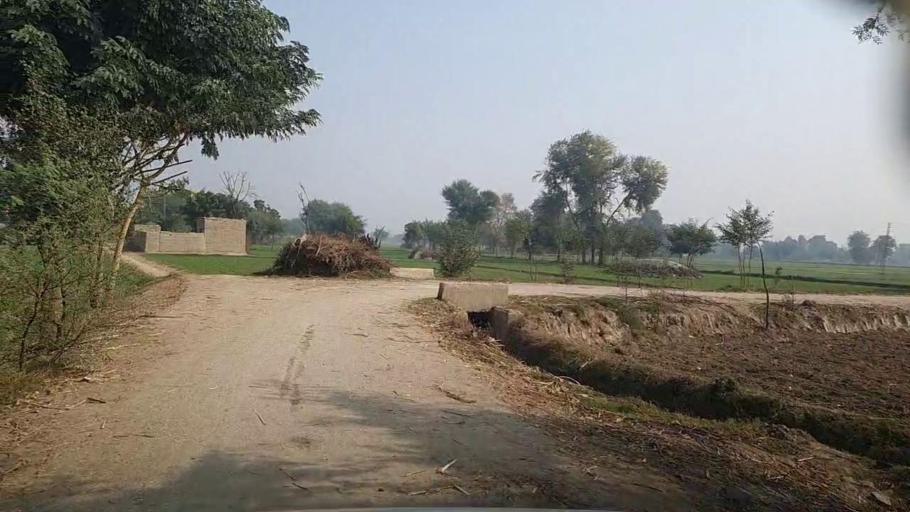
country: PK
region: Sindh
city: Setharja Old
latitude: 27.1239
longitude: 68.5156
